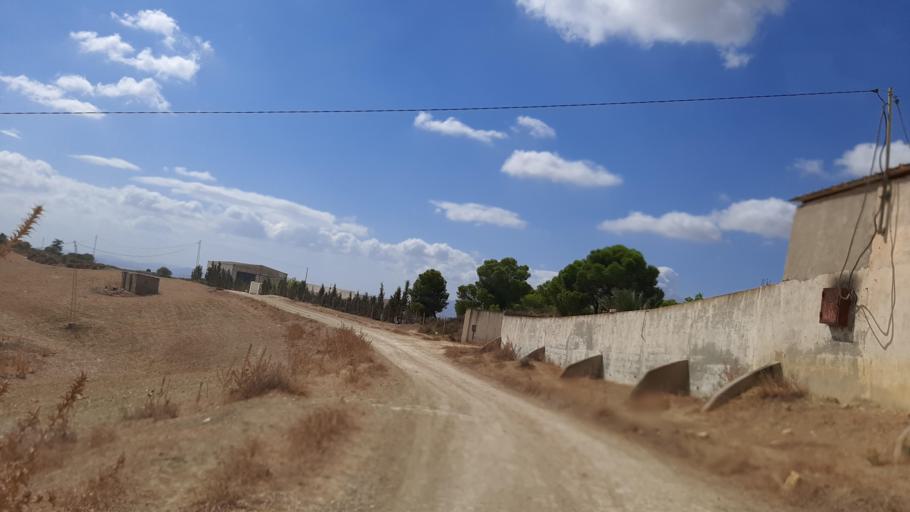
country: TN
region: Zaghwan
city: Zaghouan
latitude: 36.4894
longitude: 10.1773
